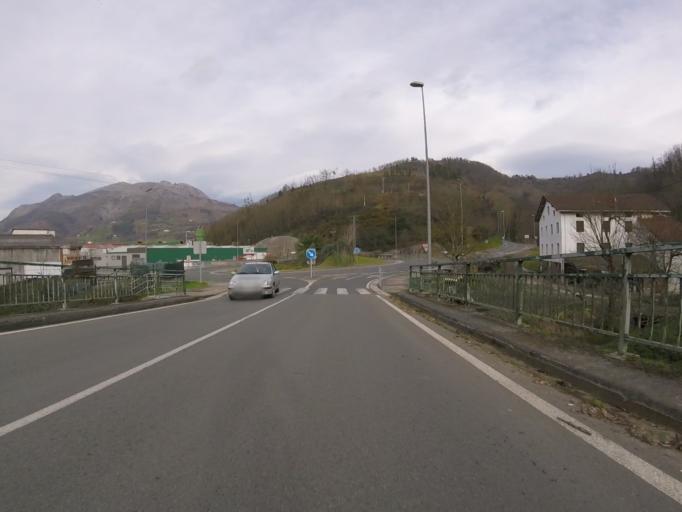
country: ES
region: Basque Country
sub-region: Provincia de Guipuzcoa
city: Azpeitia
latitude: 43.1749
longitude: -2.2516
